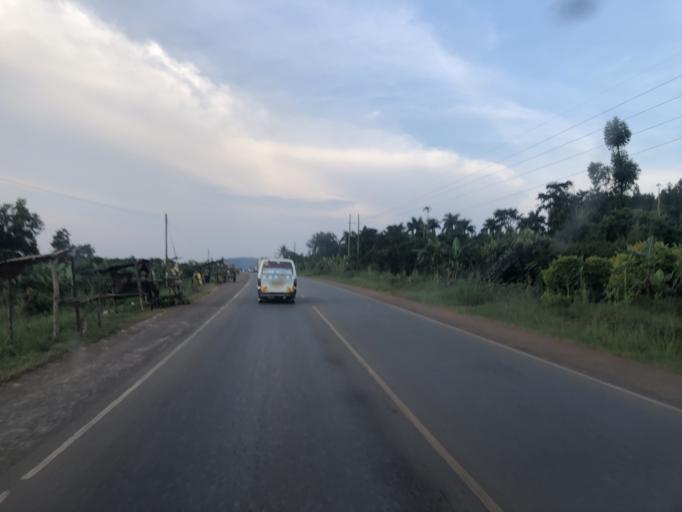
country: UG
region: Central Region
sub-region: Mpigi District
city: Mpigi
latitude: 0.2312
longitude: 32.3455
